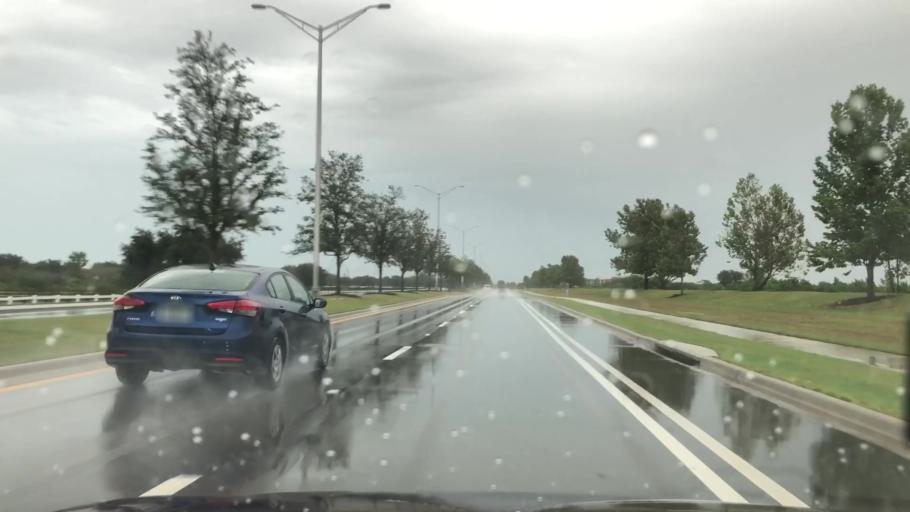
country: US
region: Florida
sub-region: Sarasota County
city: The Meadows
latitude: 27.3751
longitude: -82.3960
